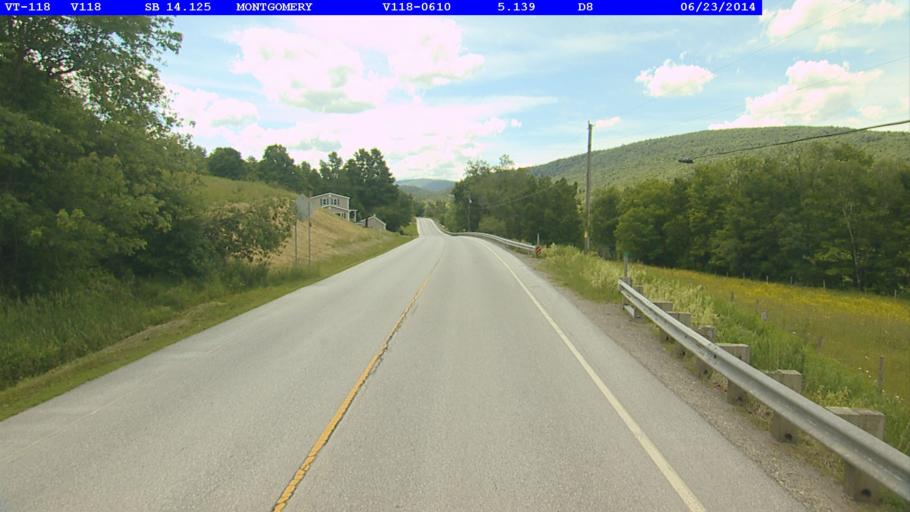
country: US
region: Vermont
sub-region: Franklin County
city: Richford
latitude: 44.8712
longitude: -72.6088
